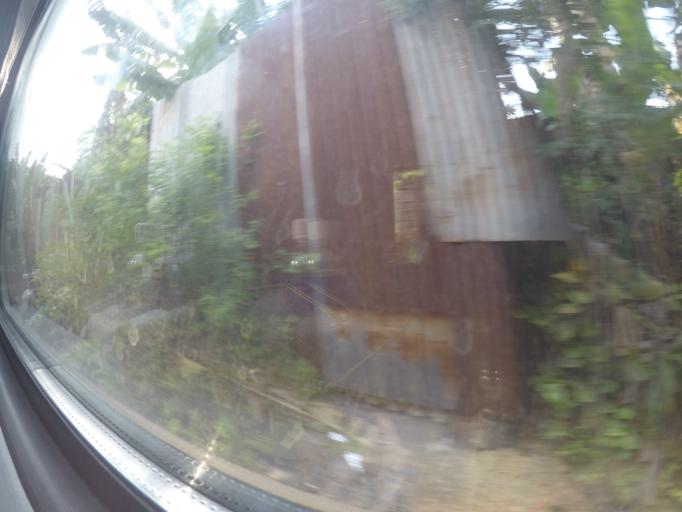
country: VN
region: Dong Nai
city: Bien Hoa
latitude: 10.9564
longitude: 106.8300
